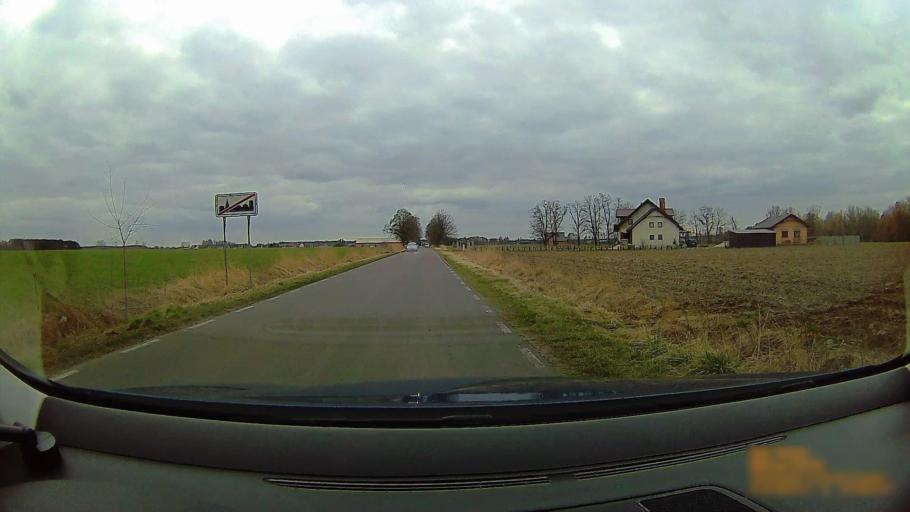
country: PL
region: Greater Poland Voivodeship
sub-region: Powiat koninski
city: Rzgow Pierwszy
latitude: 52.1435
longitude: 18.0559
